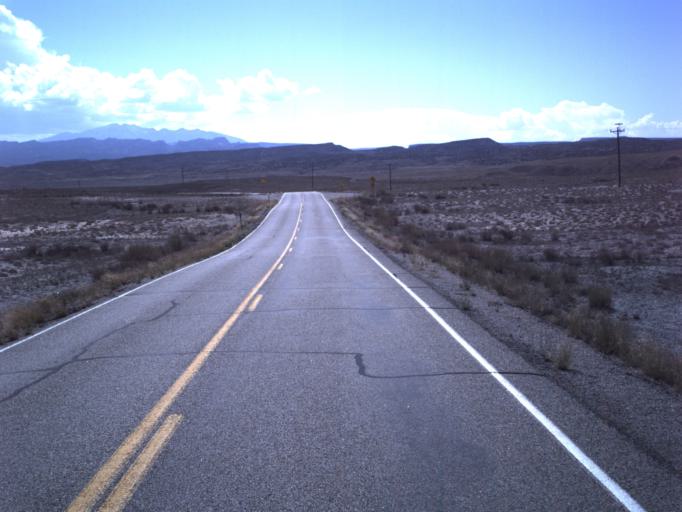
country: US
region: Utah
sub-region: Grand County
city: Moab
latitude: 38.8853
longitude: -109.3121
